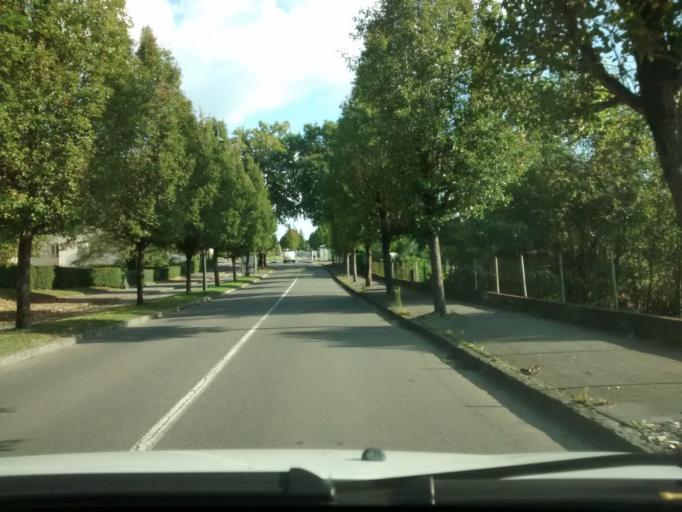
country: FR
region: Pays de la Loire
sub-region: Departement de la Loire-Atlantique
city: Orvault
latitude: 47.2716
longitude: -1.6202
